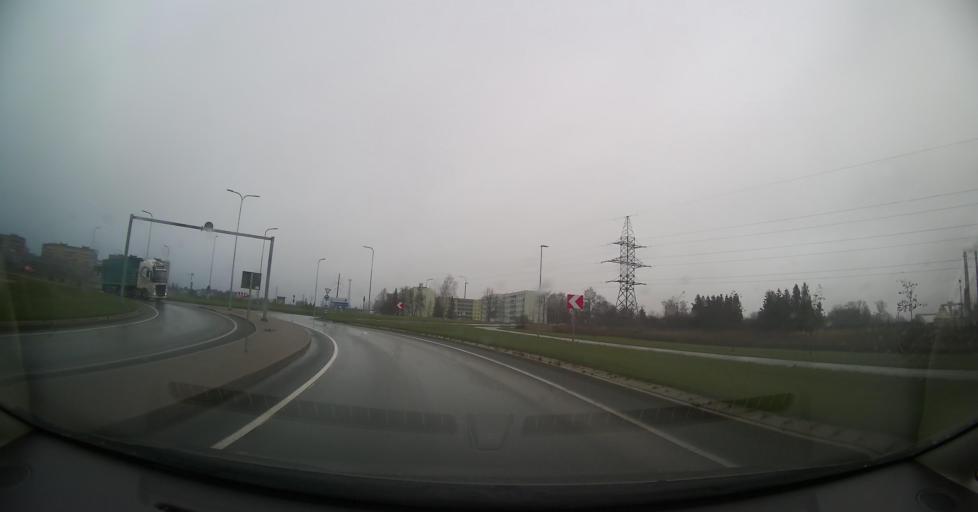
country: EE
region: Tartu
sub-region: Tartu linn
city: Tartu
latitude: 58.3689
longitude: 26.7821
